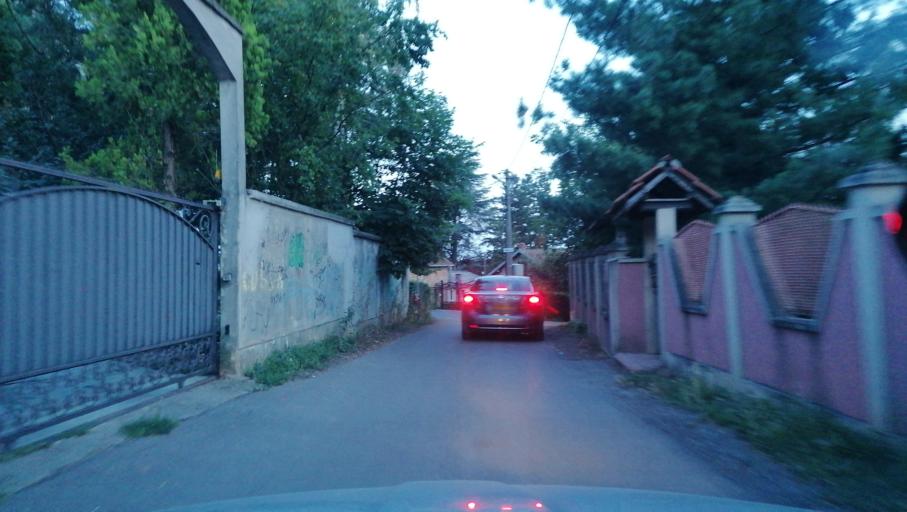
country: RS
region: Central Serbia
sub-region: Belgrade
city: Rakovica
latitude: 44.7260
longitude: 20.4839
